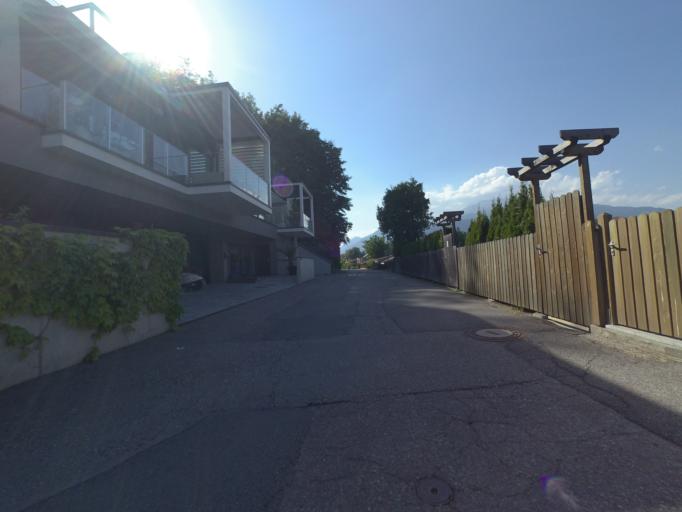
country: AT
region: Carinthia
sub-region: Politischer Bezirk Spittal an der Drau
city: Seeboden
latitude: 46.8126
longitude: 13.5137
